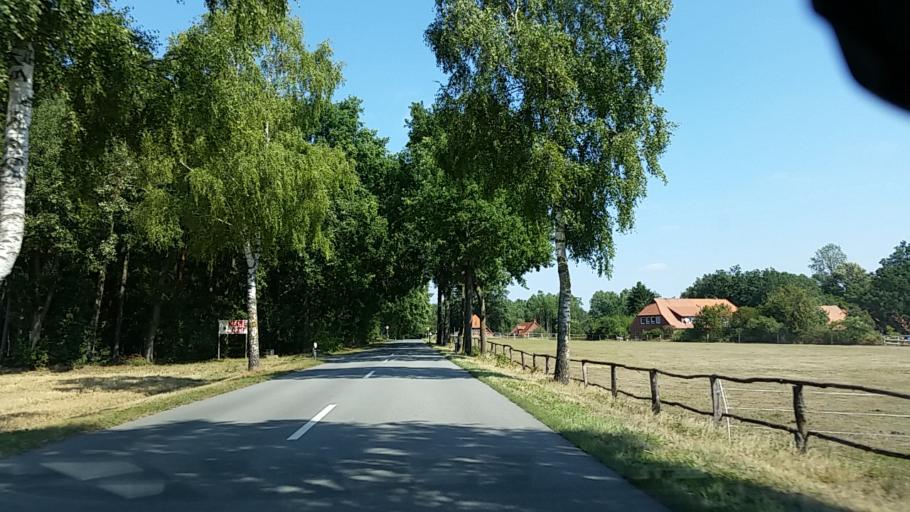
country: DE
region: Lower Saxony
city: Vastorf
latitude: 53.1751
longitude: 10.5210
